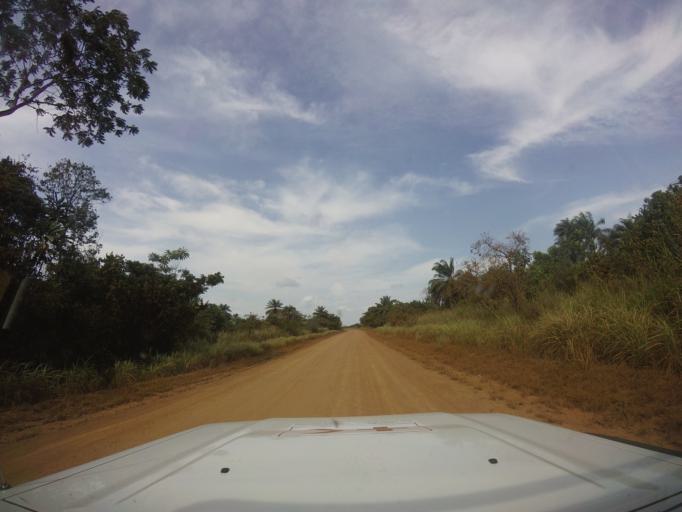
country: LR
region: Grand Cape Mount
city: Robertsport
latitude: 6.6885
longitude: -11.1170
